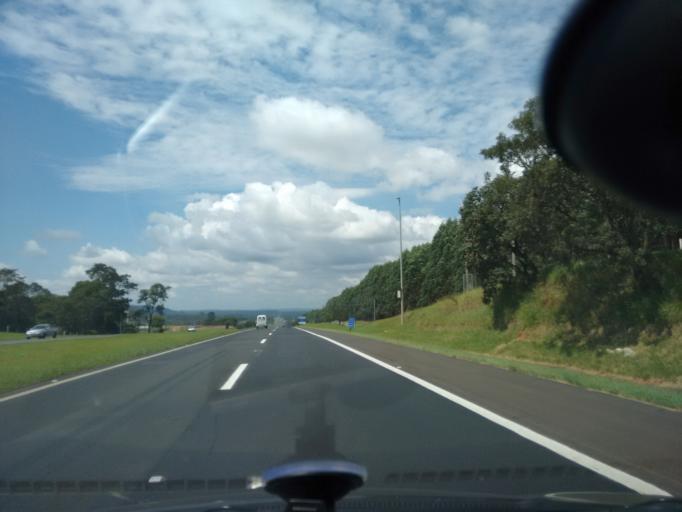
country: BR
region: Sao Paulo
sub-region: Sao Carlos
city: Sao Carlos
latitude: -22.0516
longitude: -47.8578
